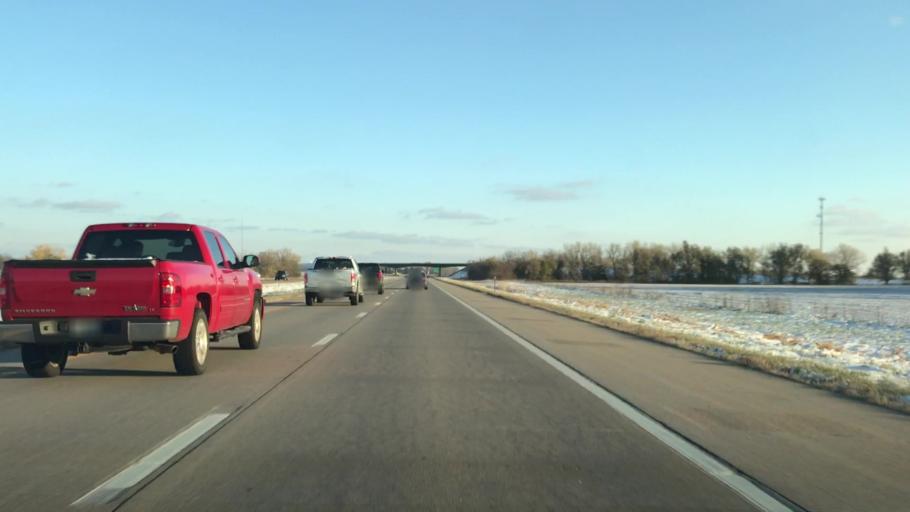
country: US
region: Kansas
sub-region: McPherson County
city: Moundridge
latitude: 38.2498
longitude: -97.5413
